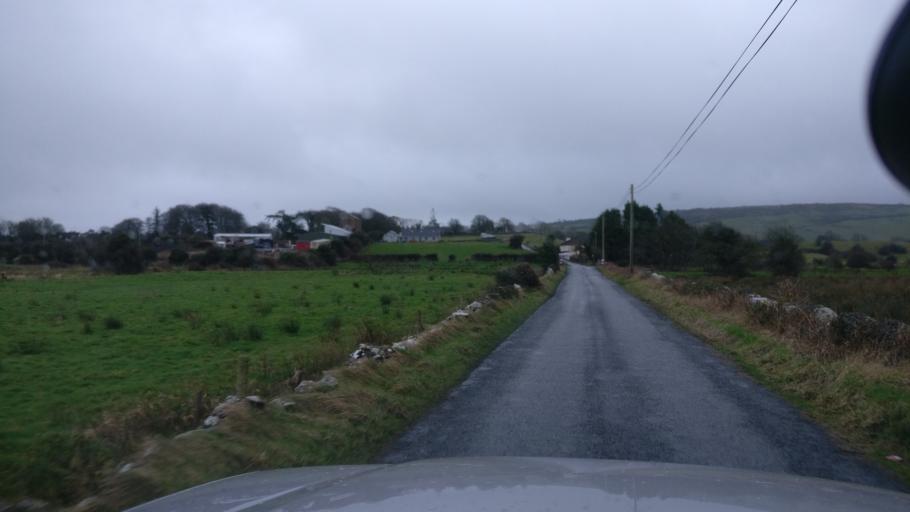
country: IE
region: Connaught
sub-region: County Galway
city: Loughrea
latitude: 53.1823
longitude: -8.6567
